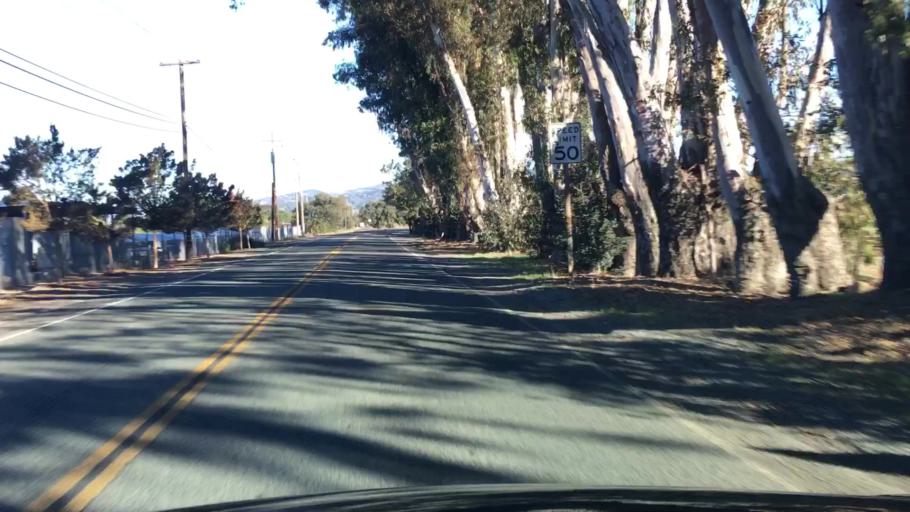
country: US
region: California
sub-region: Sonoma County
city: Sonoma
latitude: 38.2520
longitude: -122.4411
